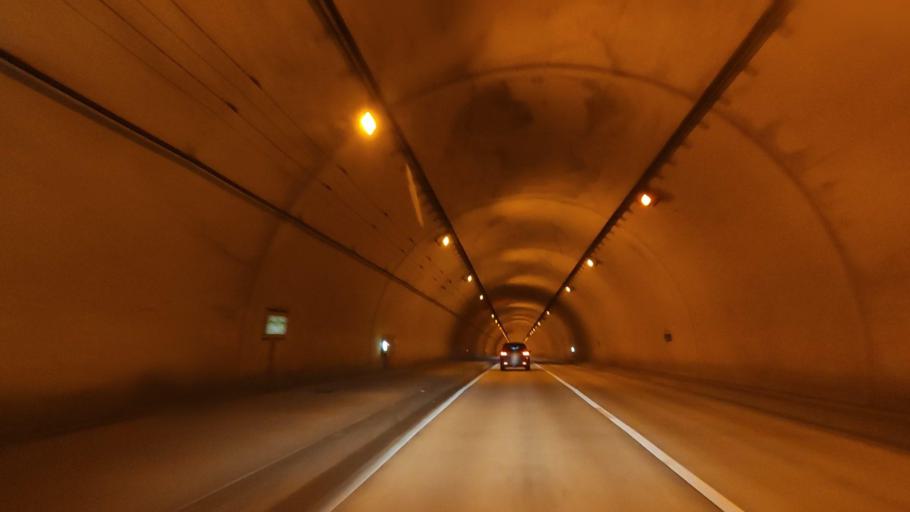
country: JP
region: Ehime
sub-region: Shikoku-chuo Shi
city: Matsuyama
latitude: 33.8824
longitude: 132.7102
